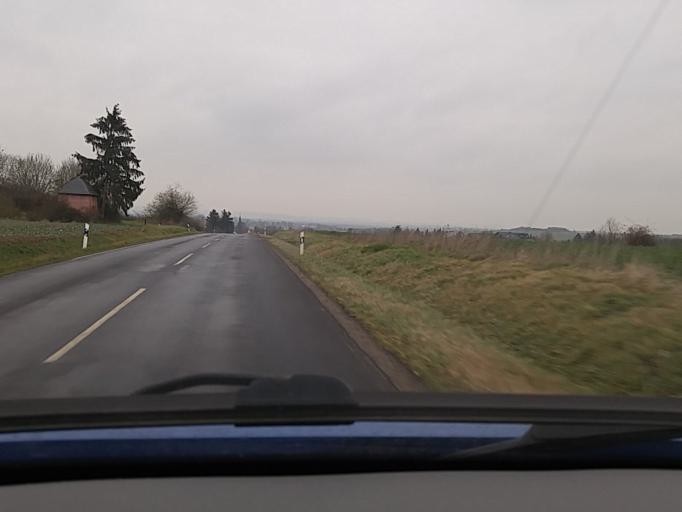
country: DE
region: Hesse
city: Reichelsheim
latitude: 50.3419
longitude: 8.9022
